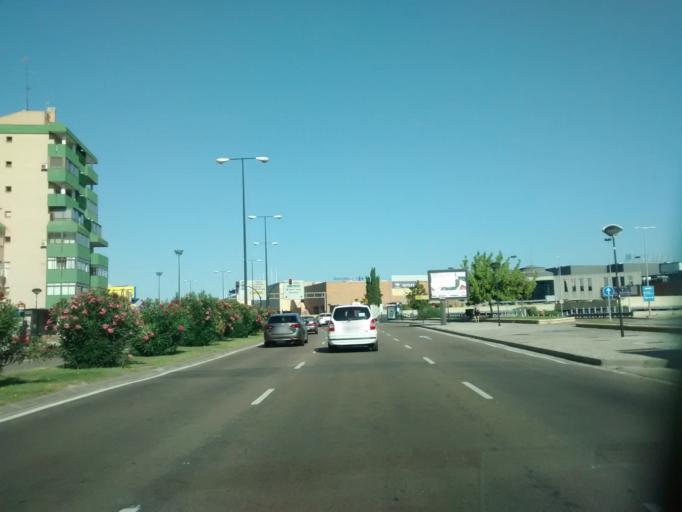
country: ES
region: Aragon
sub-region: Provincia de Zaragoza
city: Delicias
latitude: 41.6586
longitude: -0.9183
